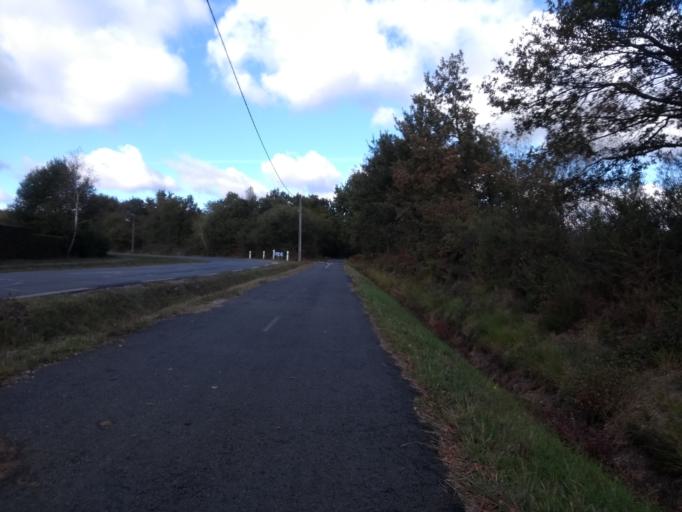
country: FR
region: Aquitaine
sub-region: Departement de la Gironde
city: Saint-Aubin-de-Medoc
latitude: 44.7976
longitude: -0.7064
